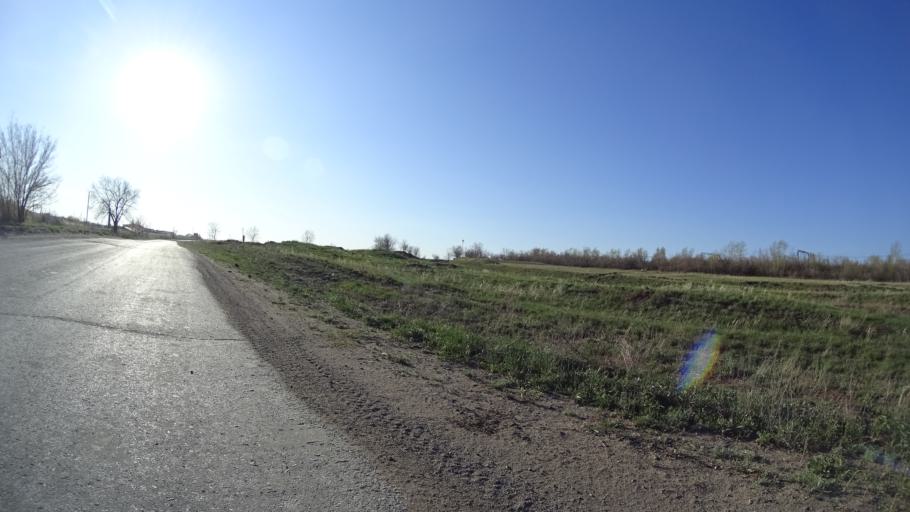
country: RU
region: Chelyabinsk
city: Troitsk
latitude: 54.0765
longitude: 61.6057
